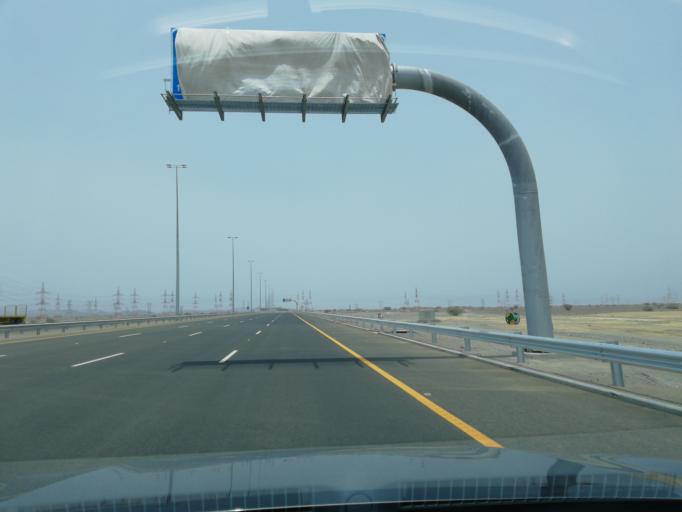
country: OM
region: Al Batinah
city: Al Liwa'
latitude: 24.4126
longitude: 56.5369
